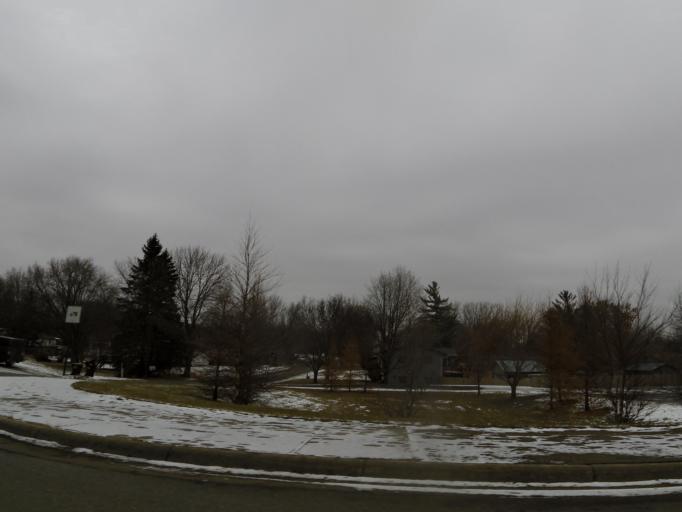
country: US
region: Minnesota
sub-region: Wright County
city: Delano
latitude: 45.0356
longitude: -93.7819
